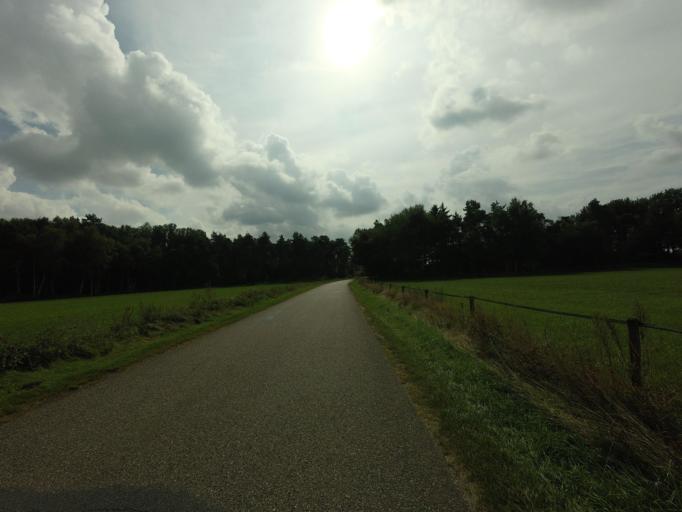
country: NL
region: Overijssel
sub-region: Gemeente Losser
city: Losser
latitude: 52.3168
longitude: 7.0304
